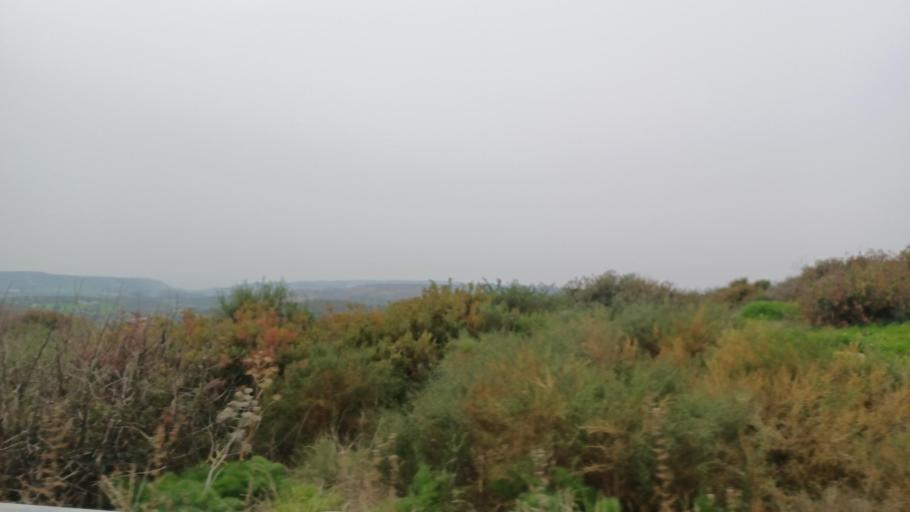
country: CY
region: Limassol
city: Pissouri
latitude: 34.7144
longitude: 32.7429
